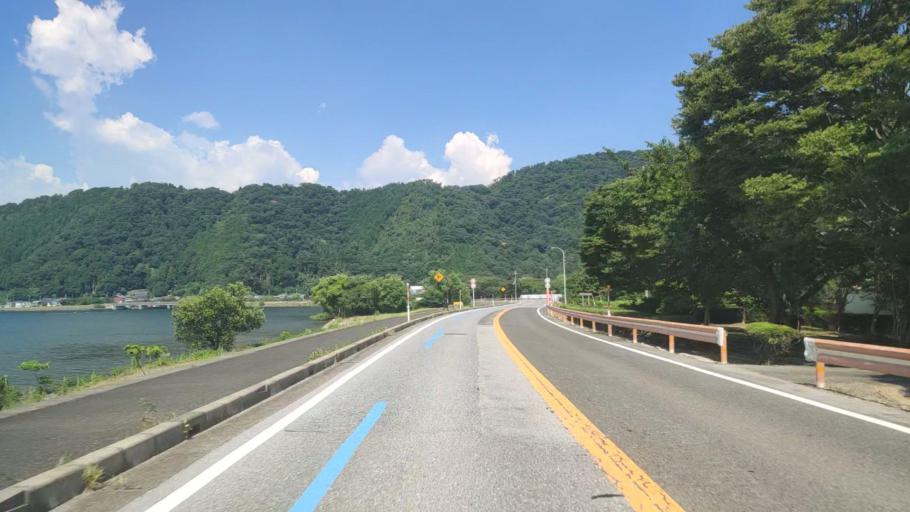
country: JP
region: Shiga Prefecture
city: Nagahama
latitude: 35.4509
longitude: 136.1932
